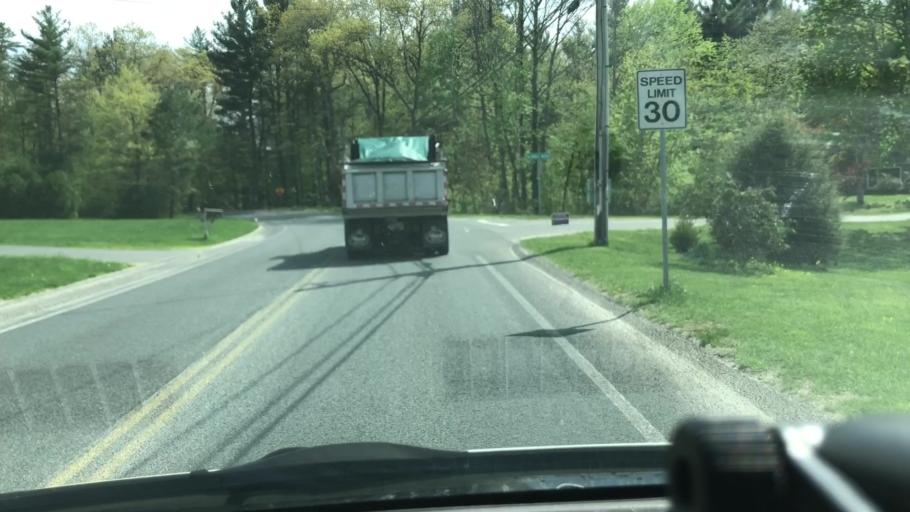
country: US
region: Massachusetts
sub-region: Hampshire County
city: Southampton
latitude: 42.2552
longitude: -72.7199
